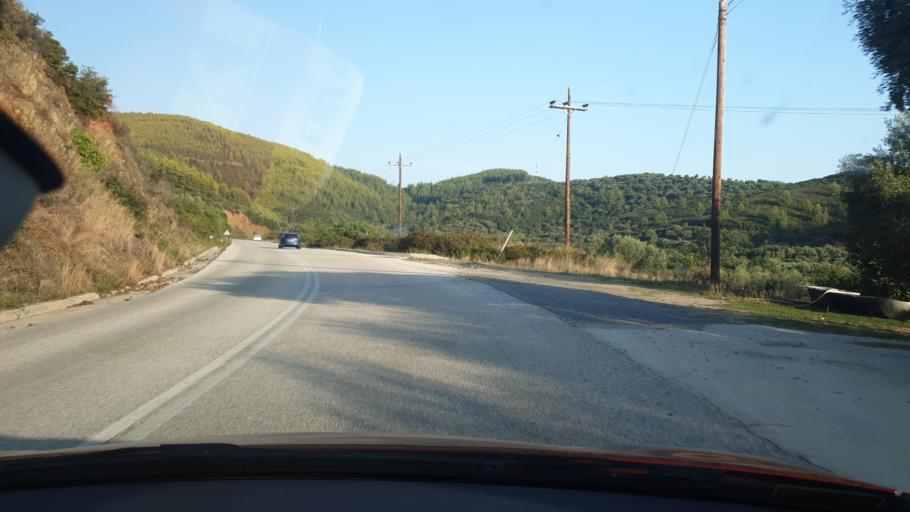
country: GR
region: Central Macedonia
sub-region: Nomos Chalkidikis
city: Sykia
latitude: 39.9811
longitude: 23.9118
